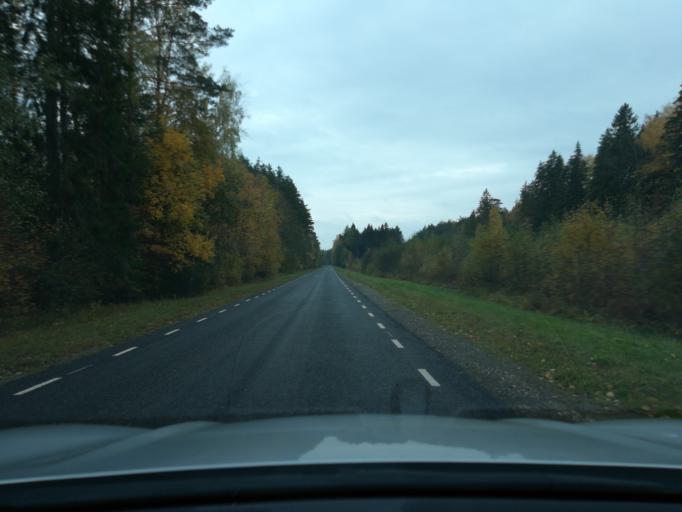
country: EE
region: Ida-Virumaa
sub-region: Johvi vald
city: Johvi
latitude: 59.0378
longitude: 27.3933
